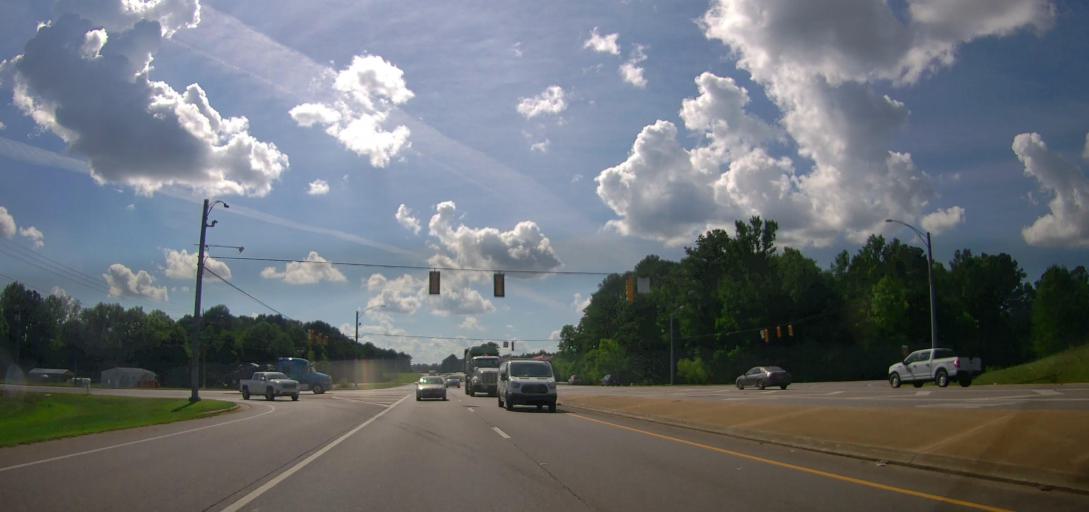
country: US
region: Alabama
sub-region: Tuscaloosa County
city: Northport
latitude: 33.2341
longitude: -87.6378
